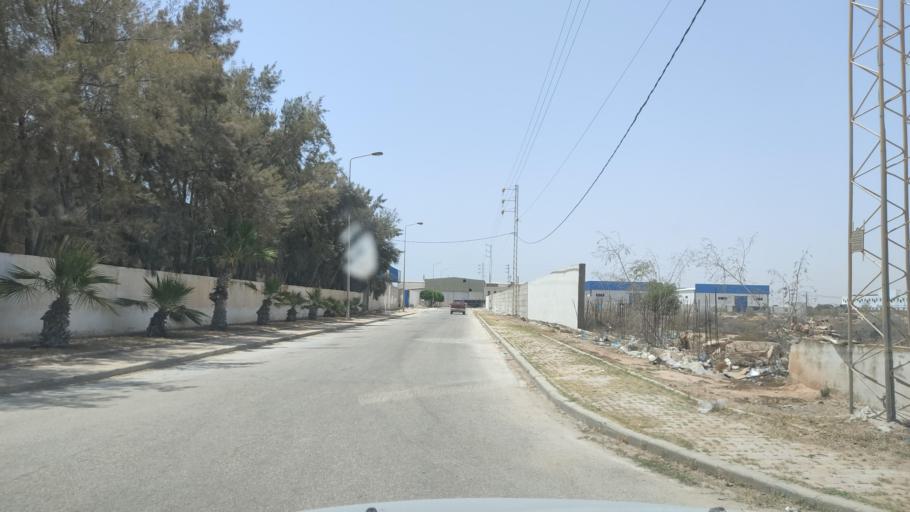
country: TN
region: Safaqis
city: Sfax
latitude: 34.6617
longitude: 10.6981
